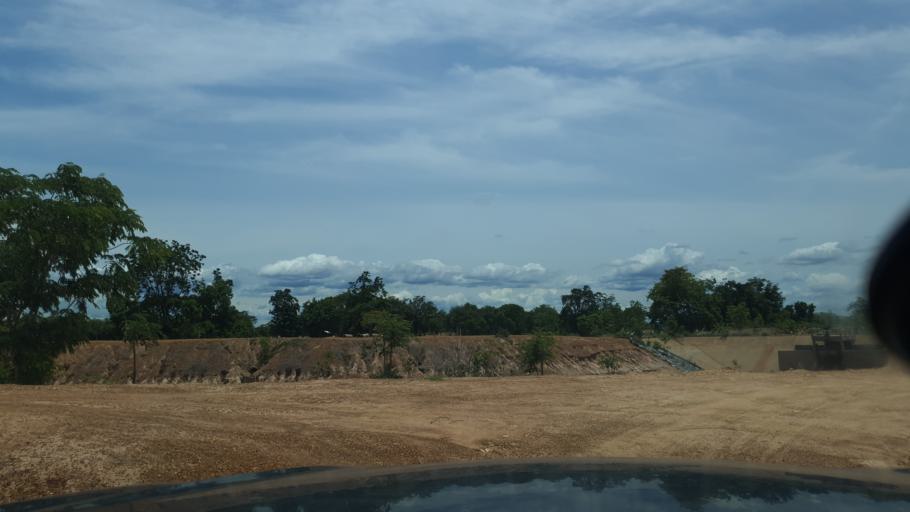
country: TH
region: Sukhothai
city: Ban Na
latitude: 17.1368
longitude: 99.6699
